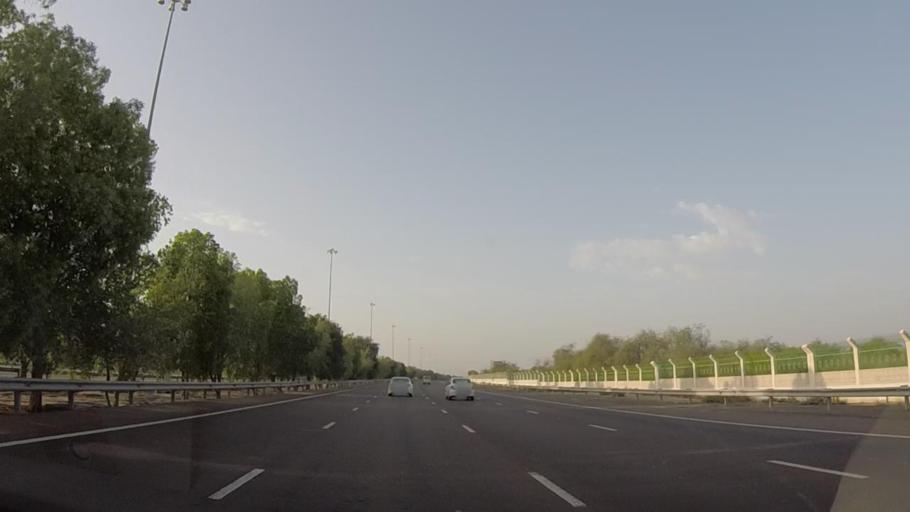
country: AE
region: Dubai
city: Dubai
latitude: 24.7697
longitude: 54.8487
